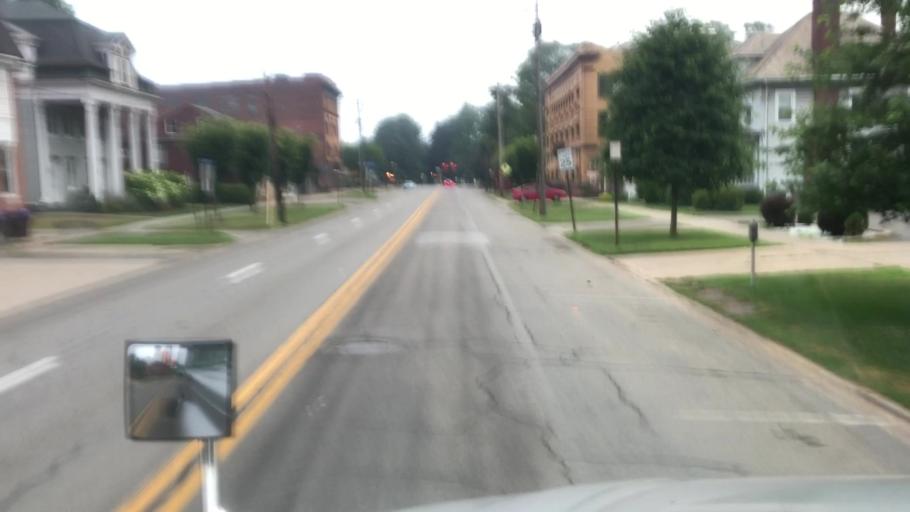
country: US
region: Pennsylvania
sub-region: Venango County
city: Franklin
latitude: 41.3954
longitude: -79.8267
